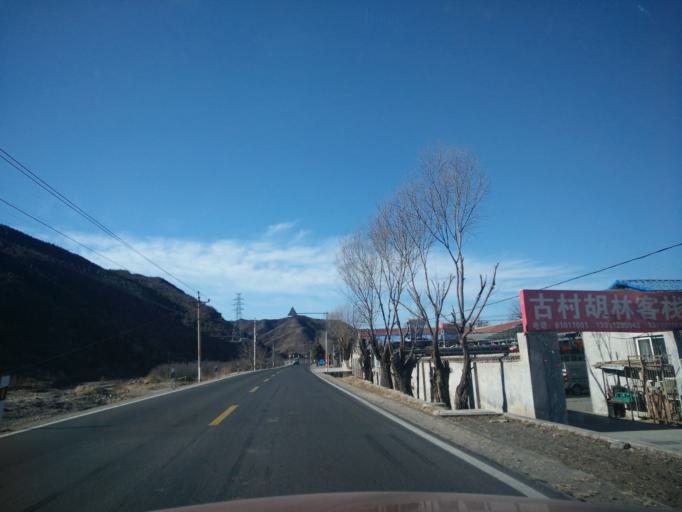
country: CN
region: Beijing
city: Zhaitang
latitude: 39.9858
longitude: 115.7486
